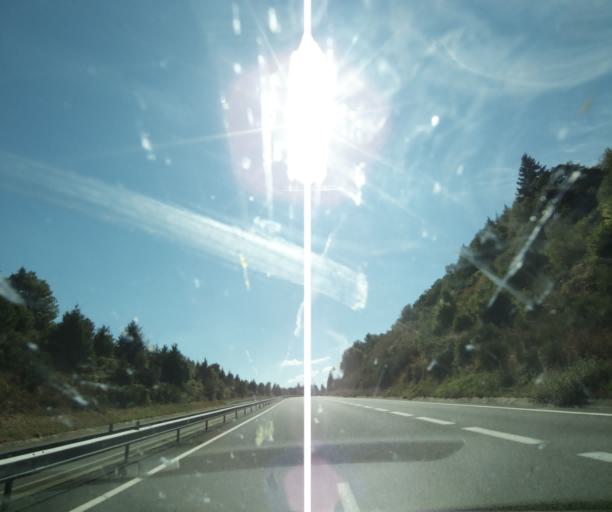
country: FR
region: Limousin
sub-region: Departement de la Correze
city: Egletons
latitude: 45.4338
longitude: 2.0447
